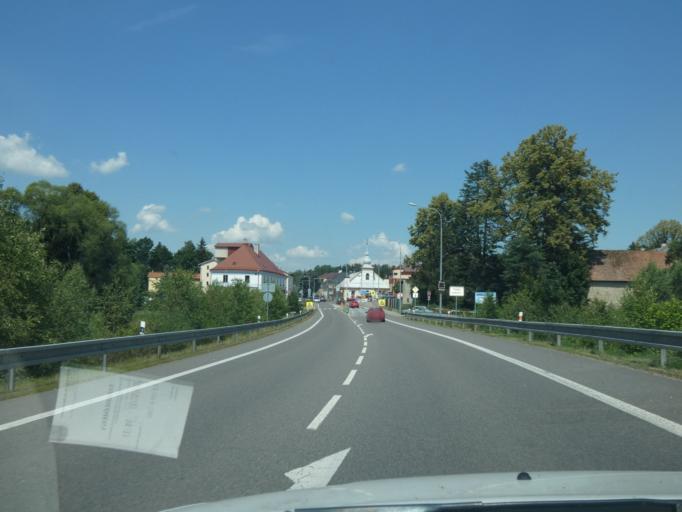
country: CZ
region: Pardubicky
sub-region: Okres Chrudim
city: Nasavrky
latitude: 49.7850
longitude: 15.8164
